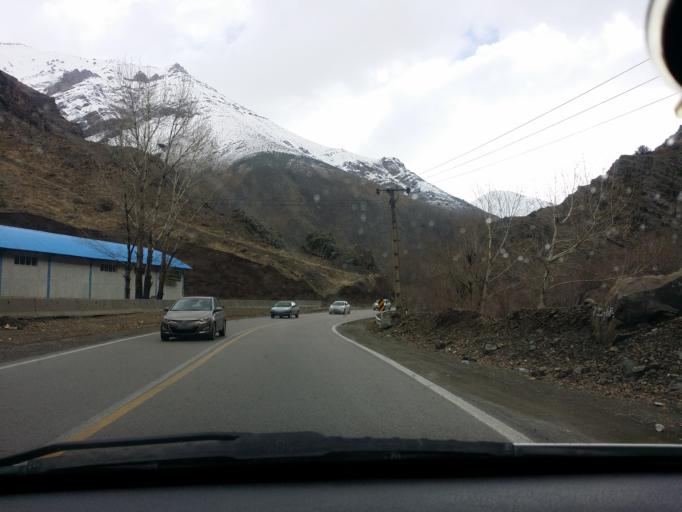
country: IR
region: Tehran
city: Tajrish
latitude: 36.0180
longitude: 51.2712
